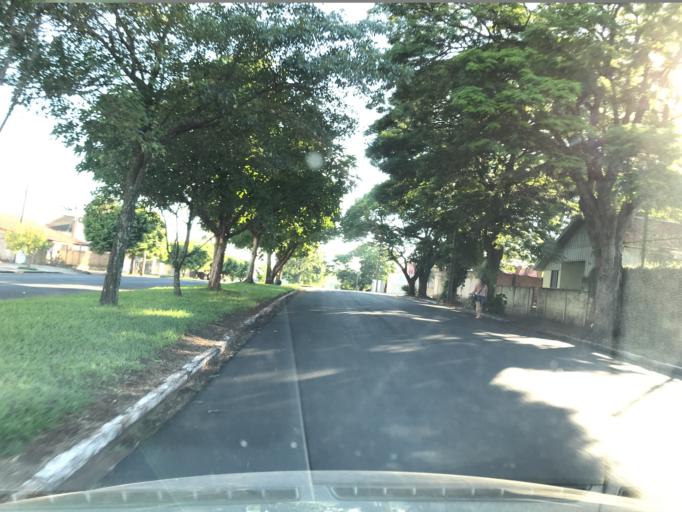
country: BR
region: Parana
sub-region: Ipora
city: Ipora
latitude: -24.0006
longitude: -53.7132
